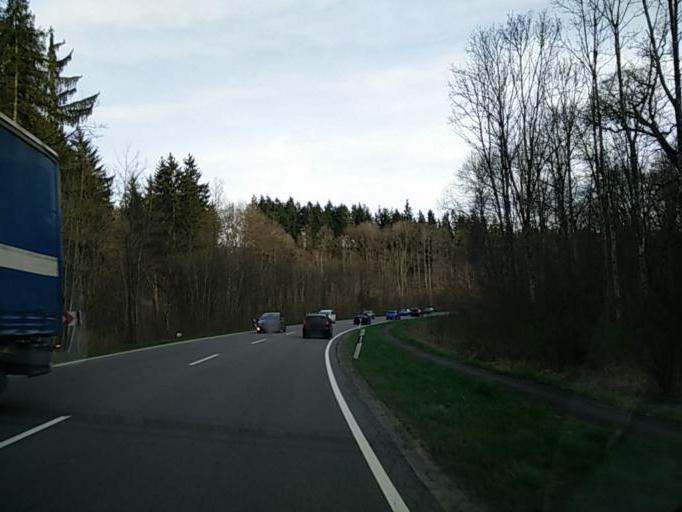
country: DE
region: Baden-Wuerttemberg
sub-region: Tuebingen Region
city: Dettenhausen
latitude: 48.5699
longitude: 9.0744
